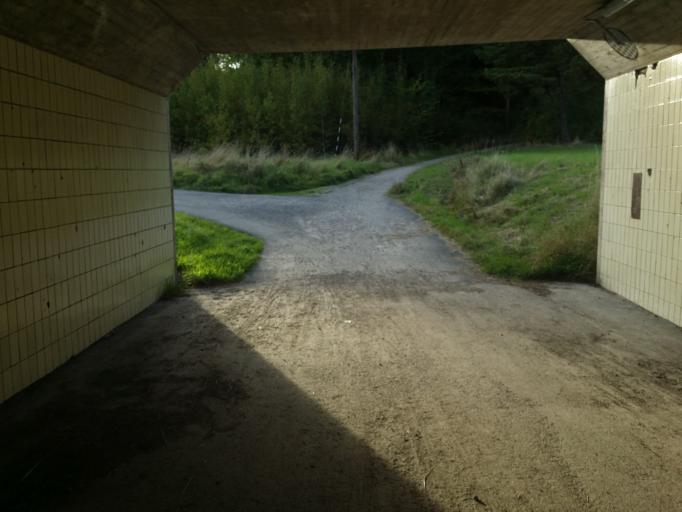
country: SE
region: Stockholm
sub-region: Upplands-Bro Kommun
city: Kungsaengen
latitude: 59.4816
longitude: 17.7292
